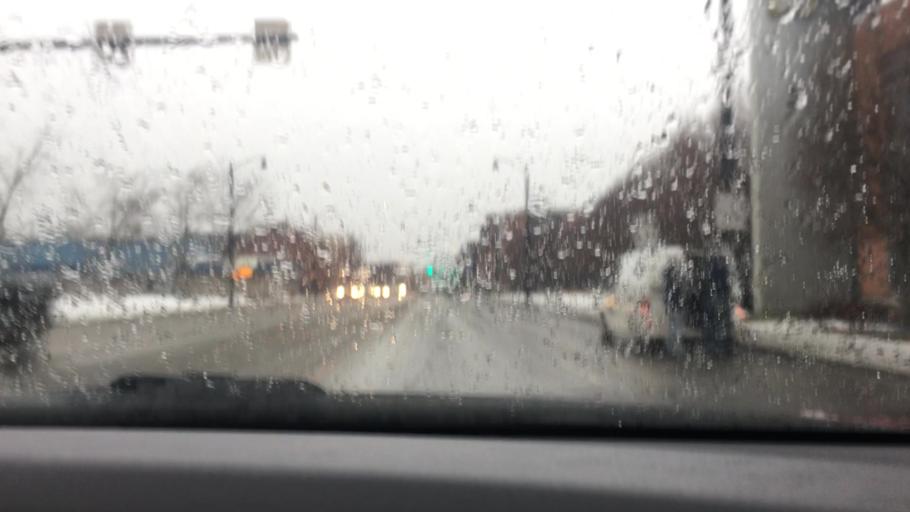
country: US
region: Pennsylvania
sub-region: Allegheny County
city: Mount Oliver
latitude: 40.4243
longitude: -79.9628
